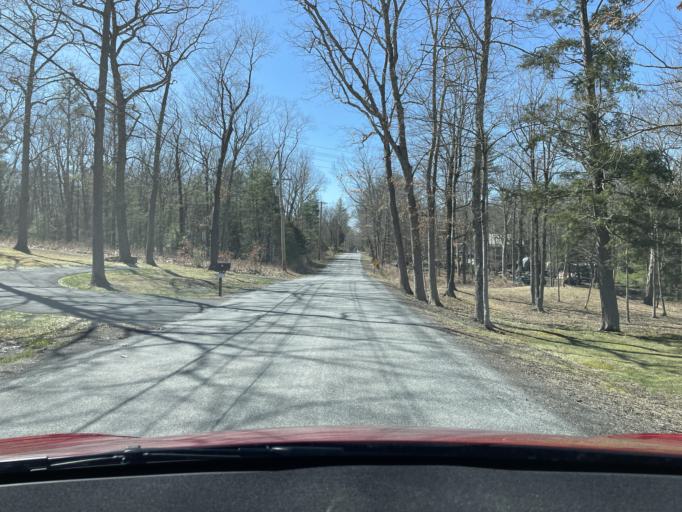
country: US
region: New York
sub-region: Ulster County
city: Manorville
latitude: 42.0721
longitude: -74.0242
